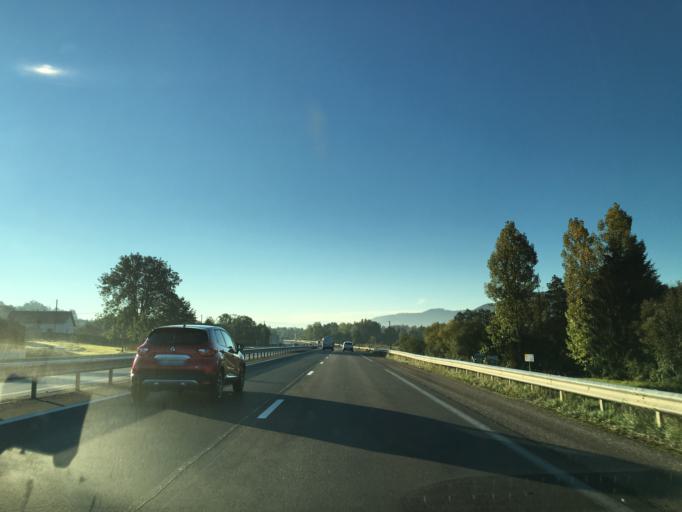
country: FR
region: Lorraine
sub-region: Departement des Vosges
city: Saint-Michel-sur-Meurthe
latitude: 48.3341
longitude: 6.8950
